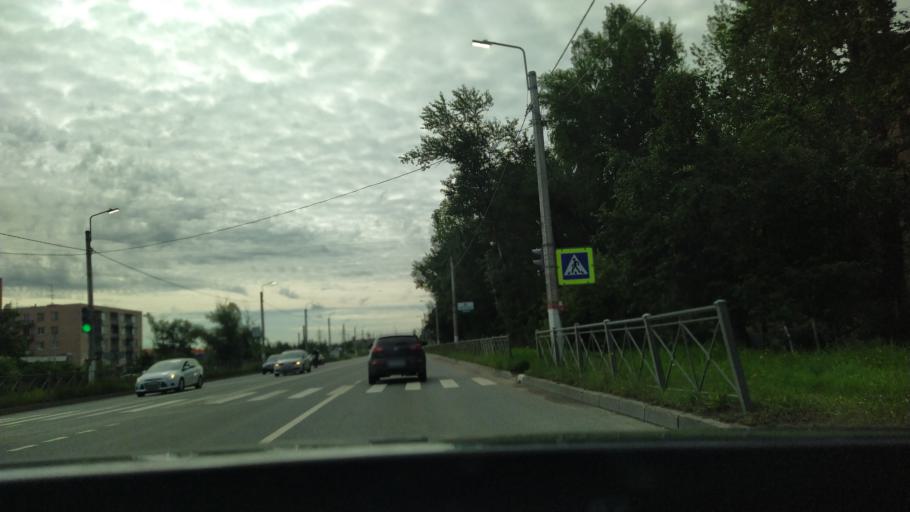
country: RU
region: Leningrad
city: Tosno
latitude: 59.5579
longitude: 30.8460
